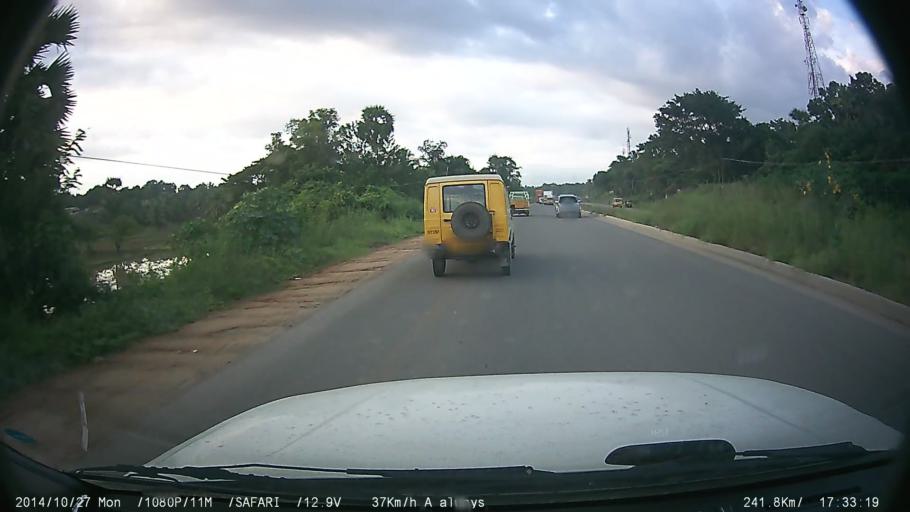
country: IN
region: Kerala
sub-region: Palakkad district
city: Palakkad
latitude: 10.6803
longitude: 76.5783
